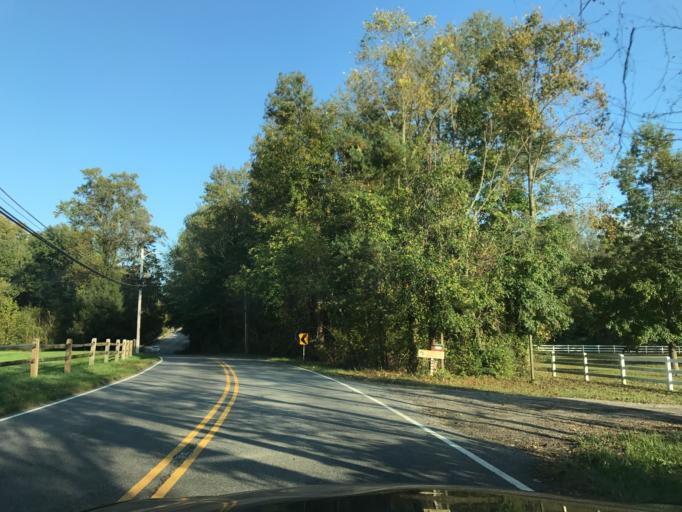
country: US
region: Maryland
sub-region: Anne Arundel County
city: Crownsville
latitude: 39.0475
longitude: -76.6281
